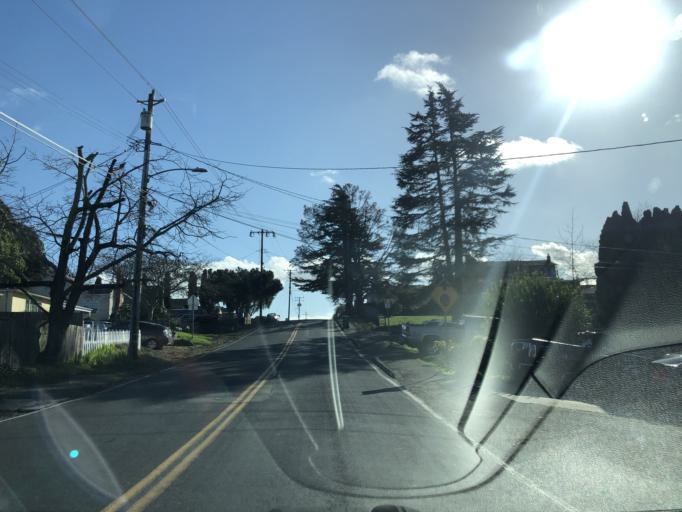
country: US
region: California
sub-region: Contra Costa County
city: El Sobrante
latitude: 37.9830
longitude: -122.3030
